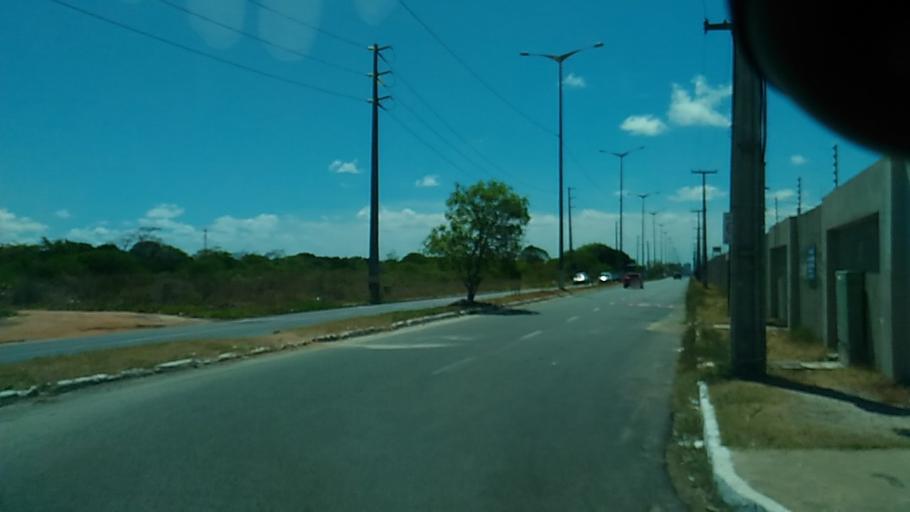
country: BR
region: Paraiba
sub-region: Joao Pessoa
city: Joao Pessoa
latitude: -7.1405
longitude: -34.8188
